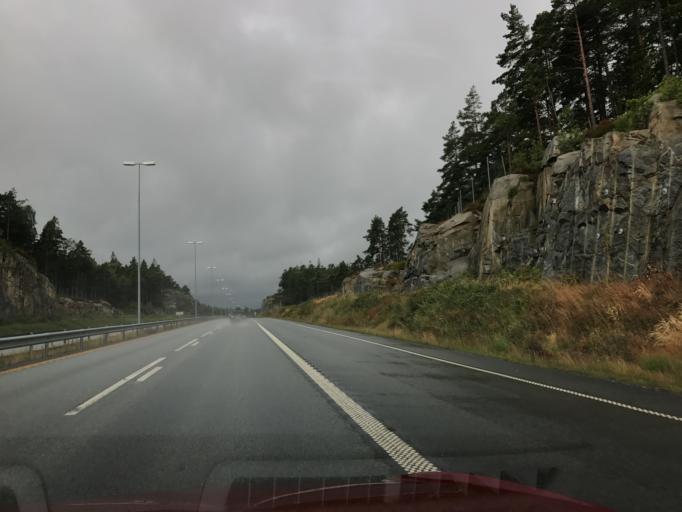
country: NO
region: Aust-Agder
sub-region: Lillesand
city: Lillesand
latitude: 58.2986
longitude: 8.4713
